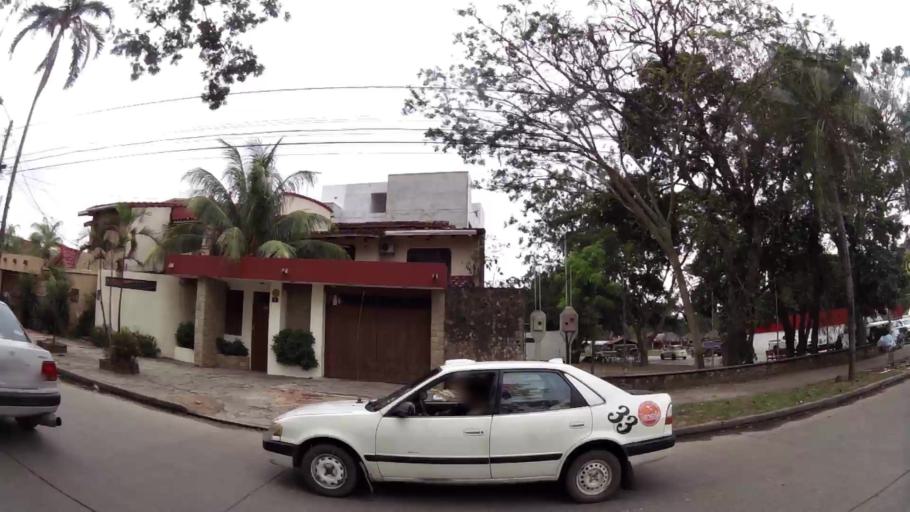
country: BO
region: Santa Cruz
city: Santa Cruz de la Sierra
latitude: -17.7689
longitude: -63.1901
